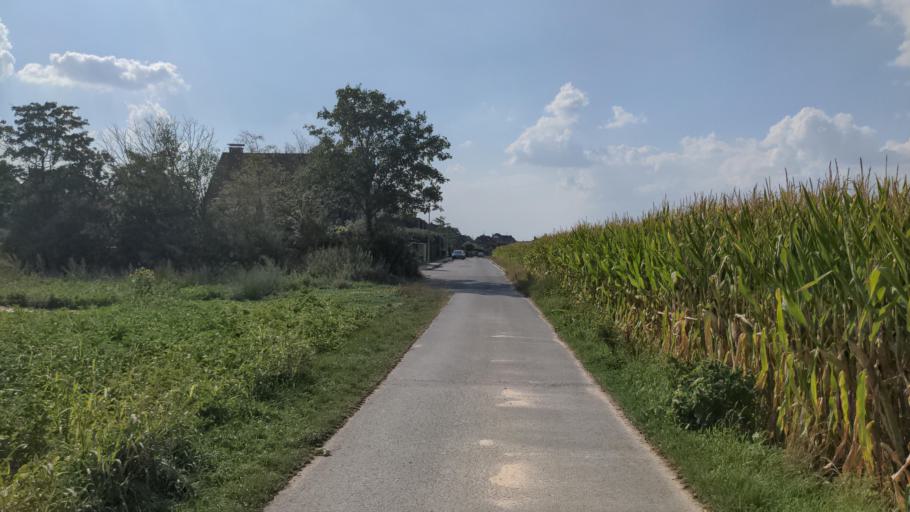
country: DE
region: North Rhine-Westphalia
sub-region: Regierungsbezirk Dusseldorf
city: Kaarst
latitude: 51.2186
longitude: 6.5772
